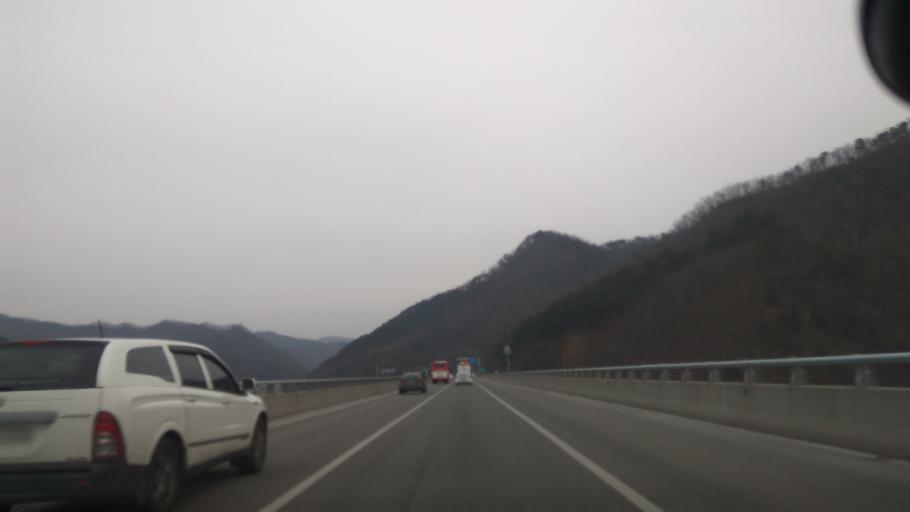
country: KR
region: Gyeonggi-do
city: Gapyeong
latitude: 37.7251
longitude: 127.5887
